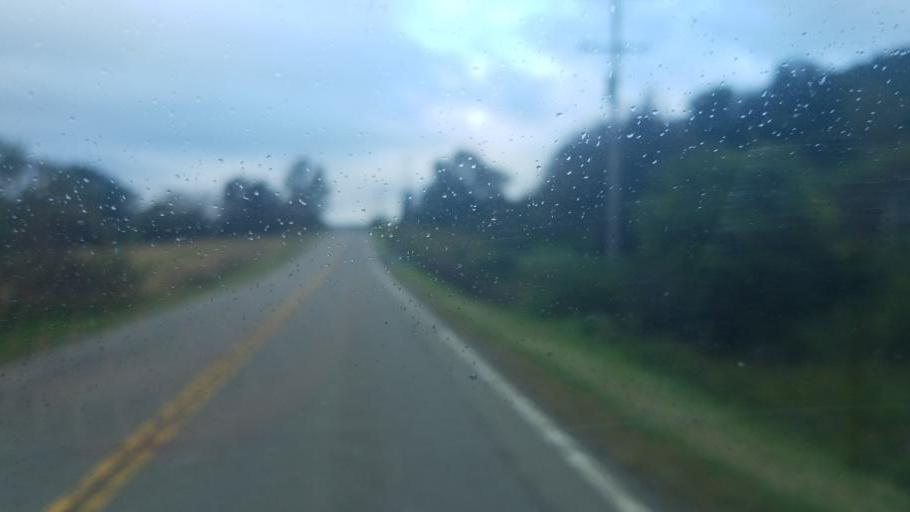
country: US
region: New York
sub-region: Allegany County
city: Cuba
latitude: 42.1886
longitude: -78.3499
